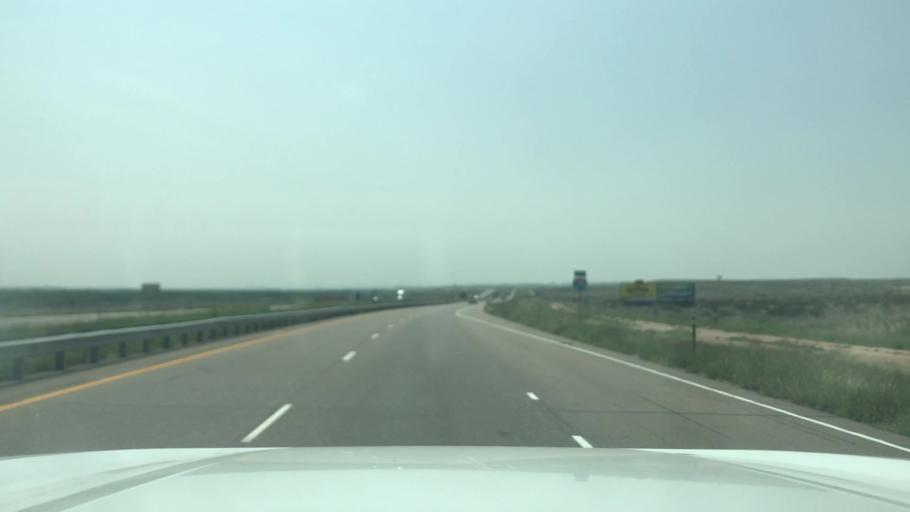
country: US
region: Colorado
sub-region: Pueblo County
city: Pueblo West
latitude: 38.3831
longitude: -104.6190
